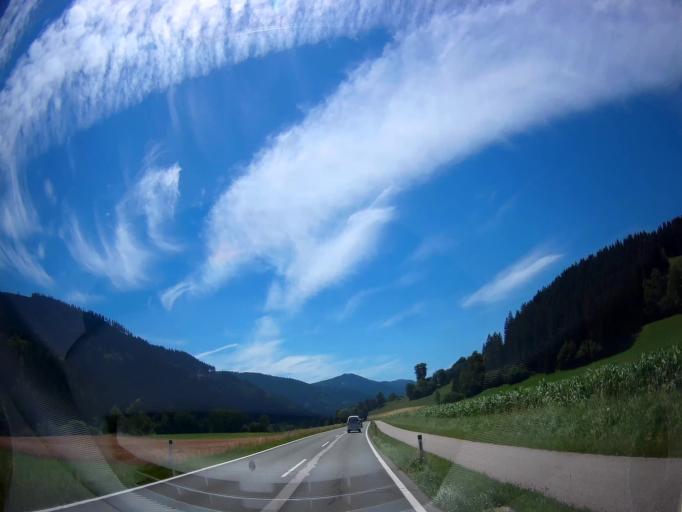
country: AT
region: Carinthia
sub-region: Politischer Bezirk Sankt Veit an der Glan
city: Strassburg
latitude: 46.8888
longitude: 14.3174
